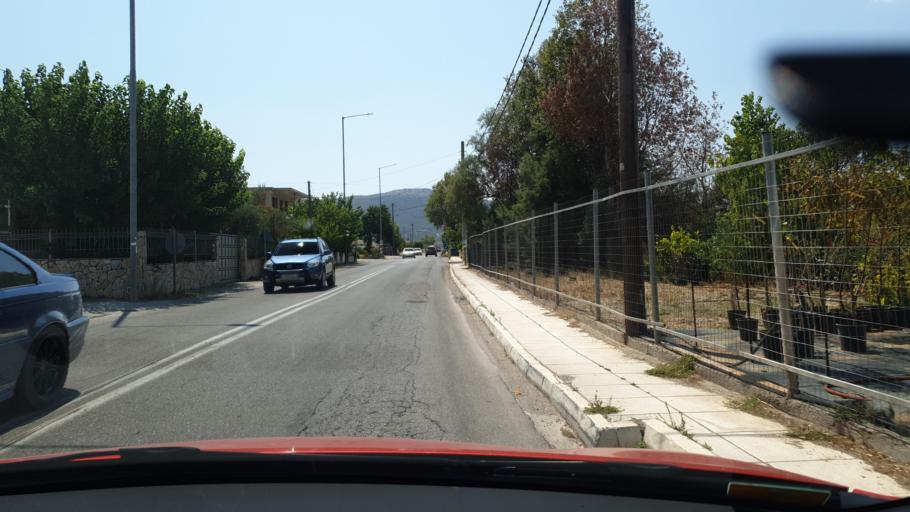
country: GR
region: Central Greece
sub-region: Nomos Evvoias
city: Aliveri
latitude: 38.4050
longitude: 24.1081
